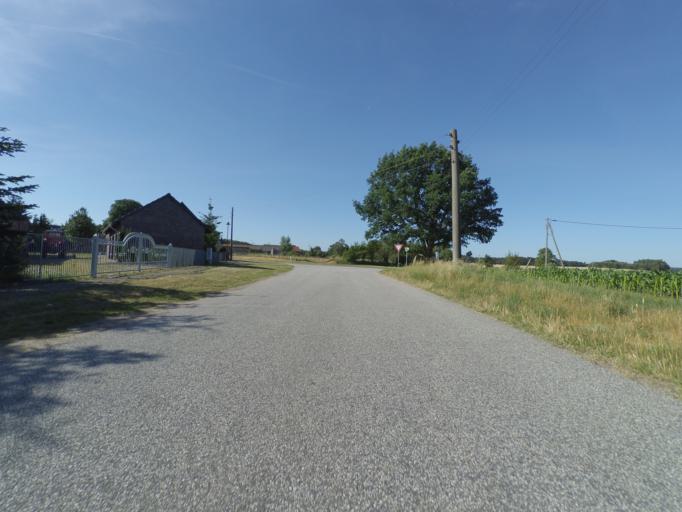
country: DE
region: Mecklenburg-Vorpommern
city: Lubz
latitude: 53.3788
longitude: 12.0301
